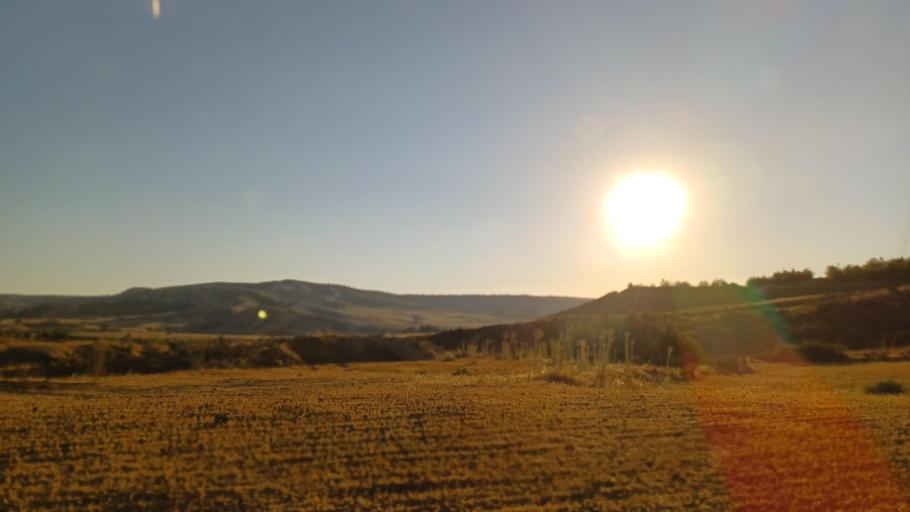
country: CY
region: Larnaka
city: Voroklini
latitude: 35.0031
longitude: 33.6406
